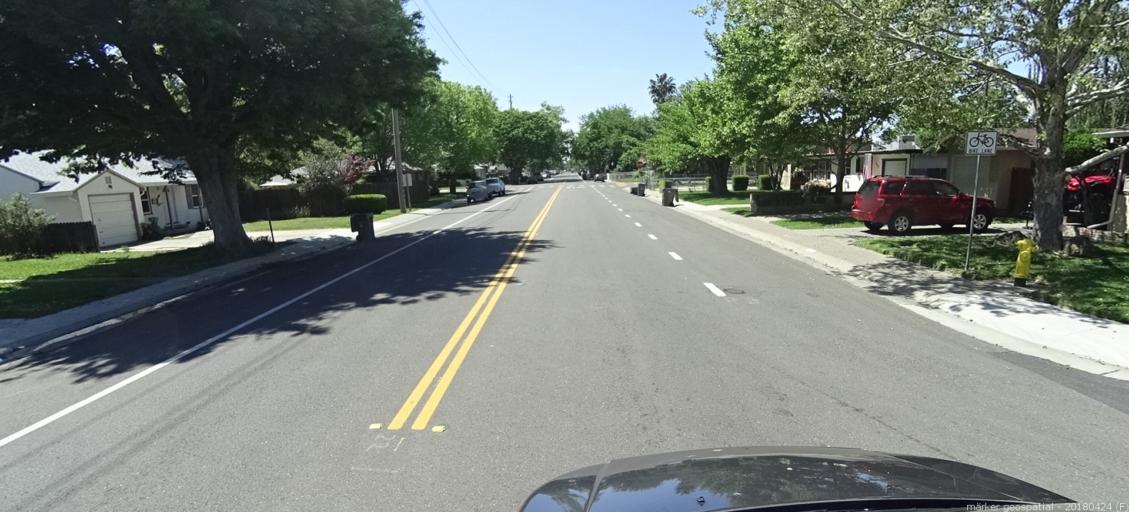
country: US
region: California
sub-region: Yolo County
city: West Sacramento
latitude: 38.5836
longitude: -121.5338
